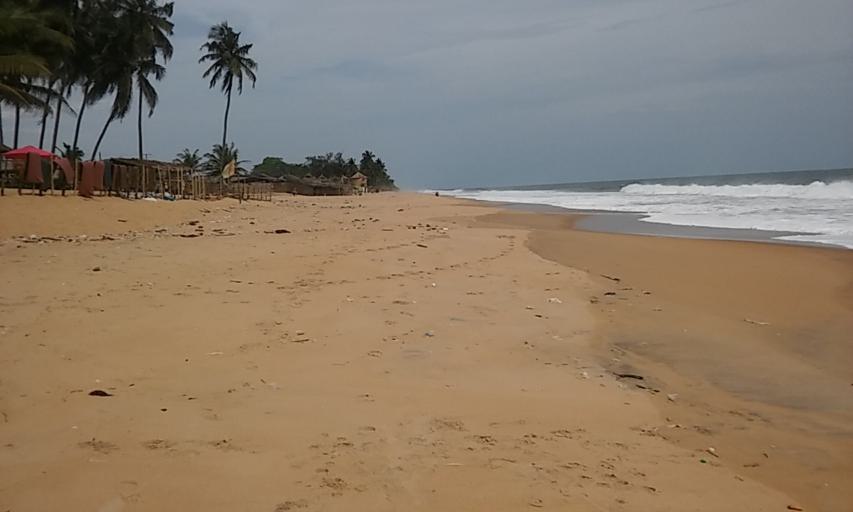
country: CI
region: Sud-Comoe
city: Grand-Bassam
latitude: 5.1969
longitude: -3.7517
